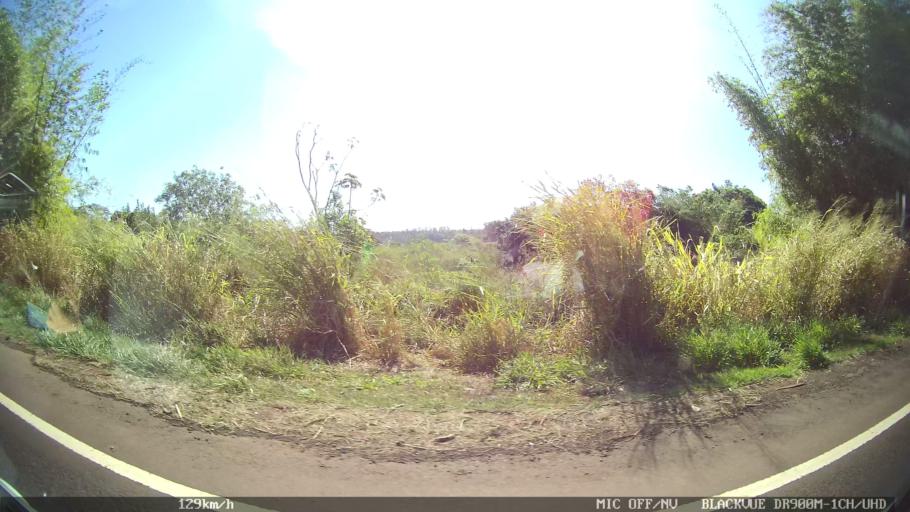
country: BR
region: Sao Paulo
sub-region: Barretos
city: Barretos
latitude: -20.6146
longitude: -48.7581
